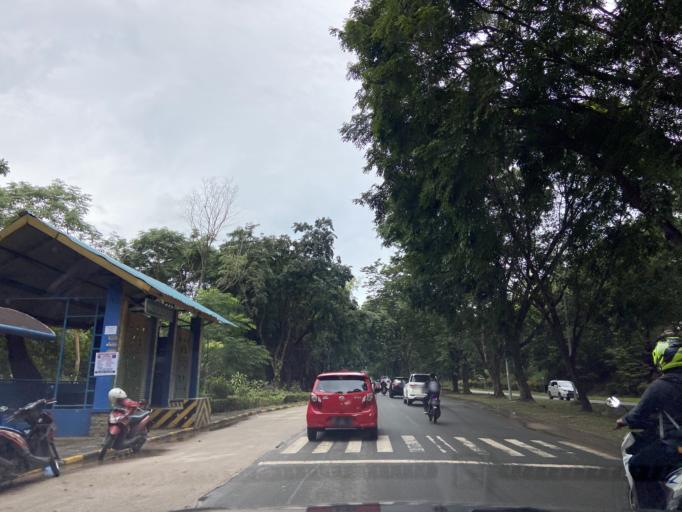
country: SG
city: Singapore
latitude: 1.1088
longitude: 103.9508
